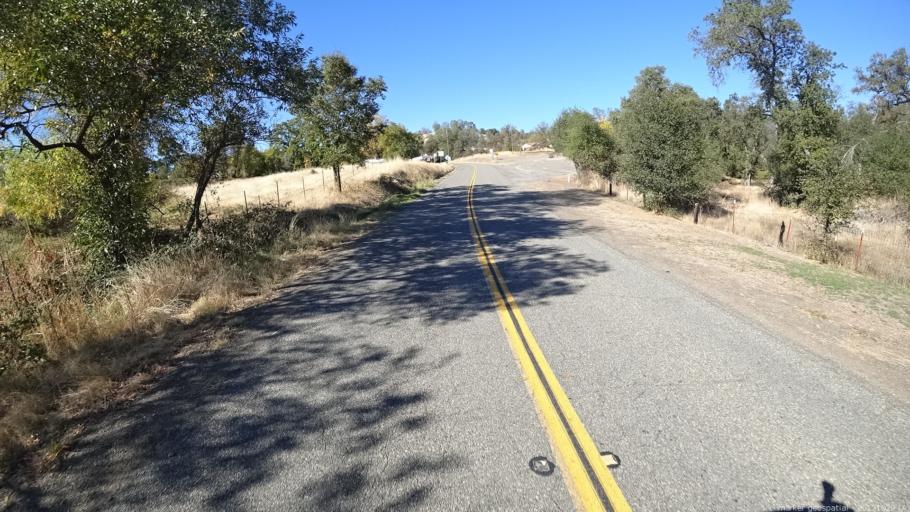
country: US
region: California
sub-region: Shasta County
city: Shasta
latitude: 40.4742
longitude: -122.6169
